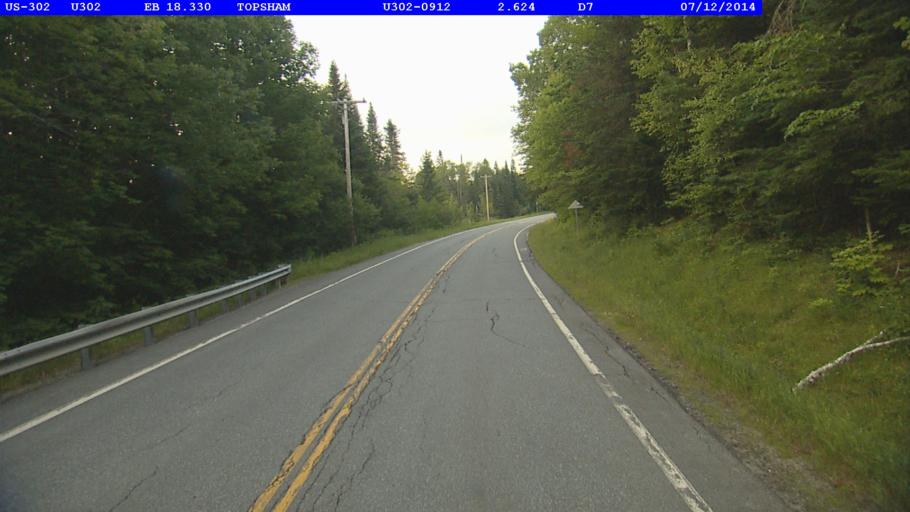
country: US
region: Vermont
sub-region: Washington County
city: Barre
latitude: 44.1736
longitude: -72.3032
